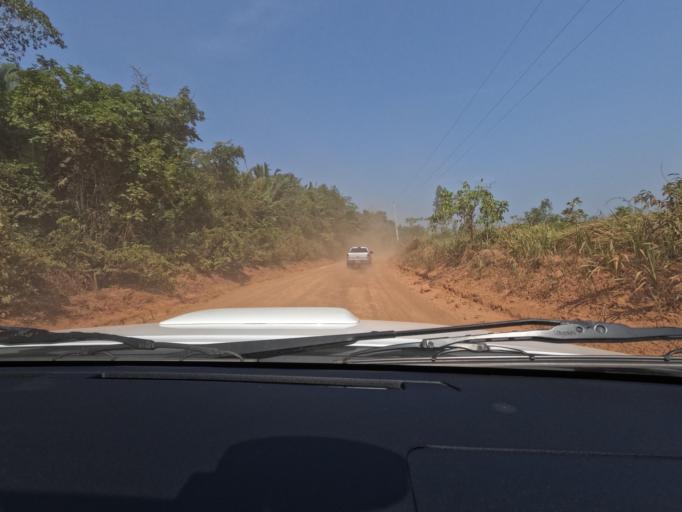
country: BR
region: Rondonia
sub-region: Porto Velho
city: Porto Velho
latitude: -8.6711
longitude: -63.9989
